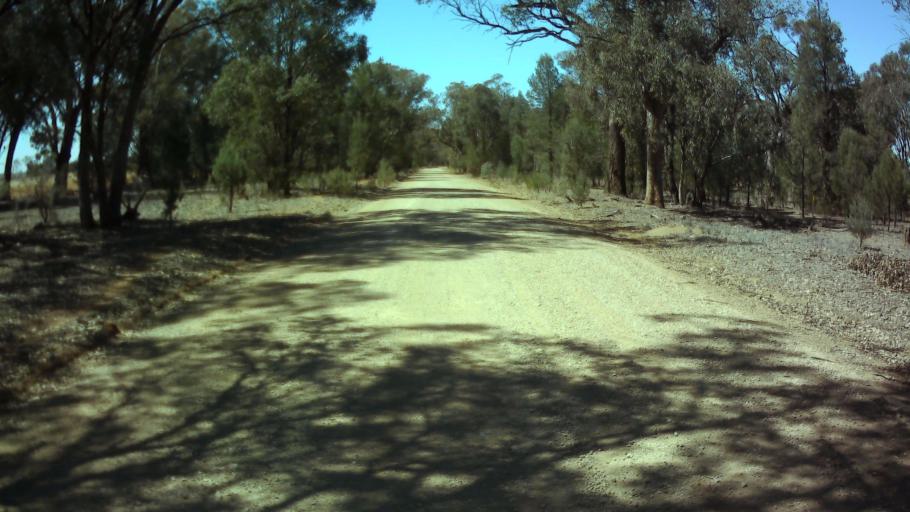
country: AU
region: New South Wales
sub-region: Weddin
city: Grenfell
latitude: -33.8591
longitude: 148.0869
